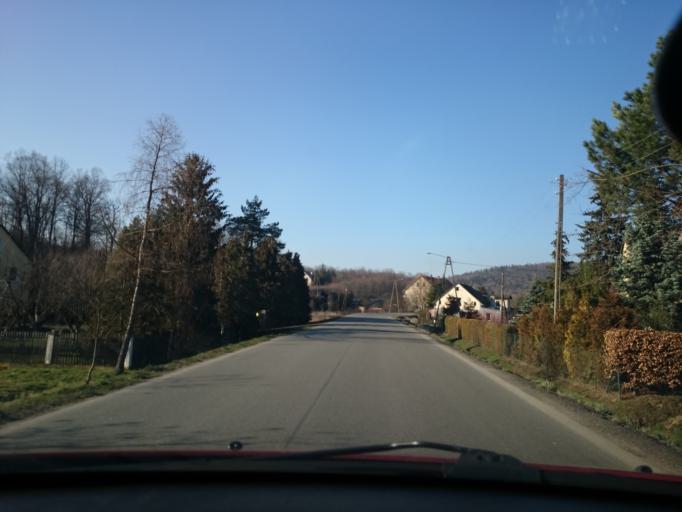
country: PL
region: Lower Silesian Voivodeship
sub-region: Powiat klodzki
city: Klodzko
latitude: 50.3899
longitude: 16.6260
